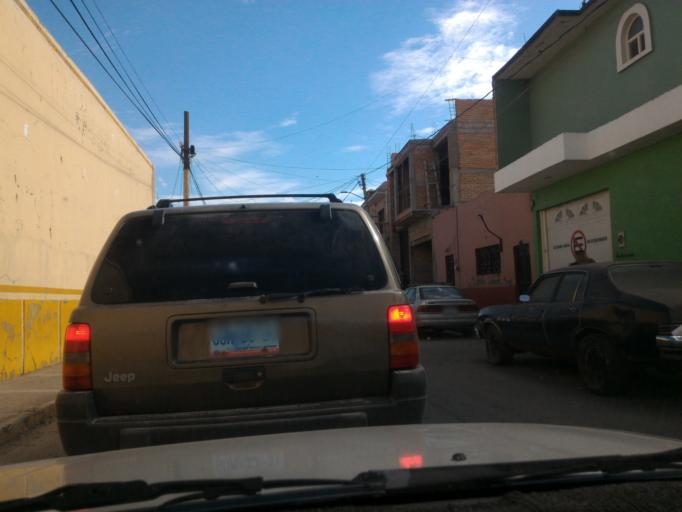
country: MX
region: Guanajuato
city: Ciudad Manuel Doblado
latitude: 20.7295
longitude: -101.9521
